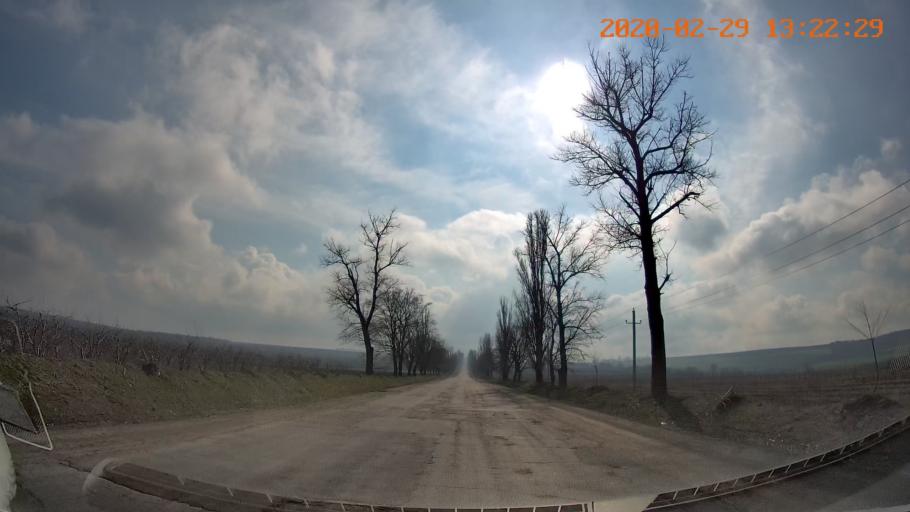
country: MD
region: Telenesti
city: Camenca
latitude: 47.9599
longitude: 28.6278
